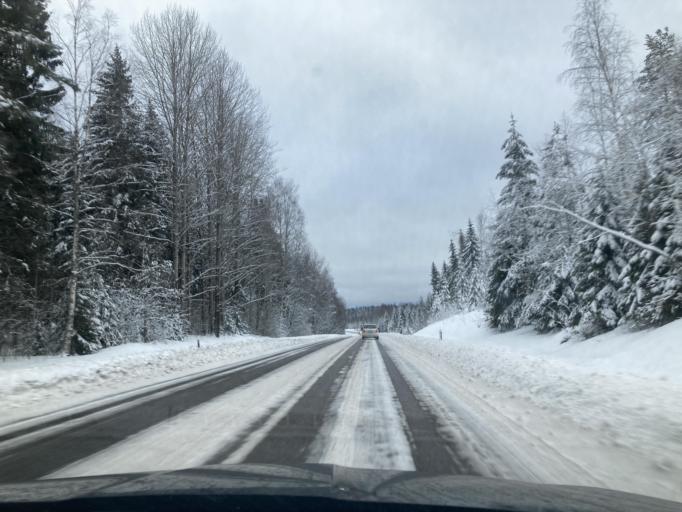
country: FI
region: Central Finland
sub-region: Jaemsae
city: Kuhmoinen
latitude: 61.5069
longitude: 25.1397
